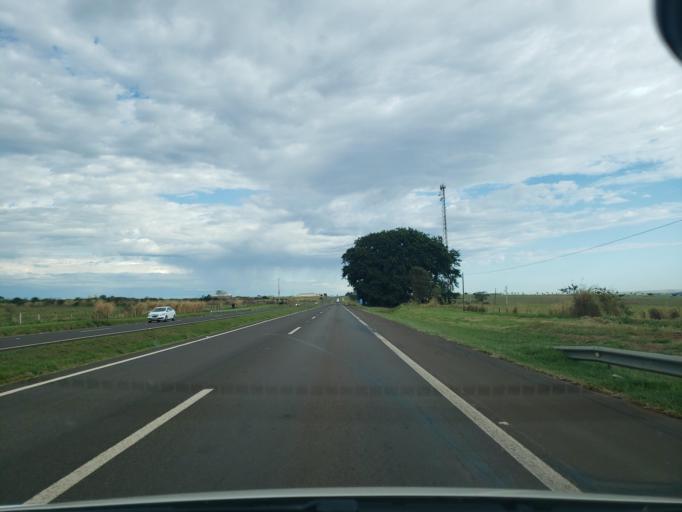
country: BR
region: Sao Paulo
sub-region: Jau
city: Jau
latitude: -22.2681
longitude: -48.4956
